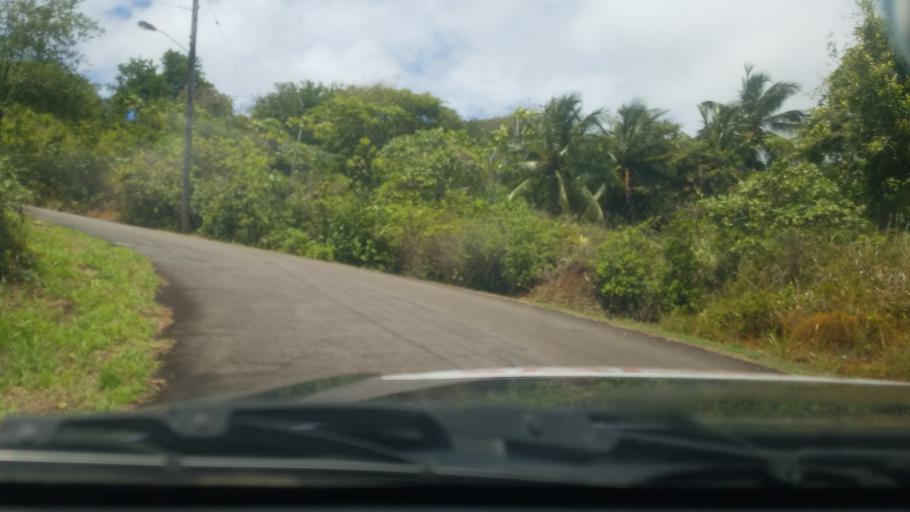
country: LC
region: Dennery Quarter
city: Dennery
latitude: 13.8983
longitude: -60.8957
